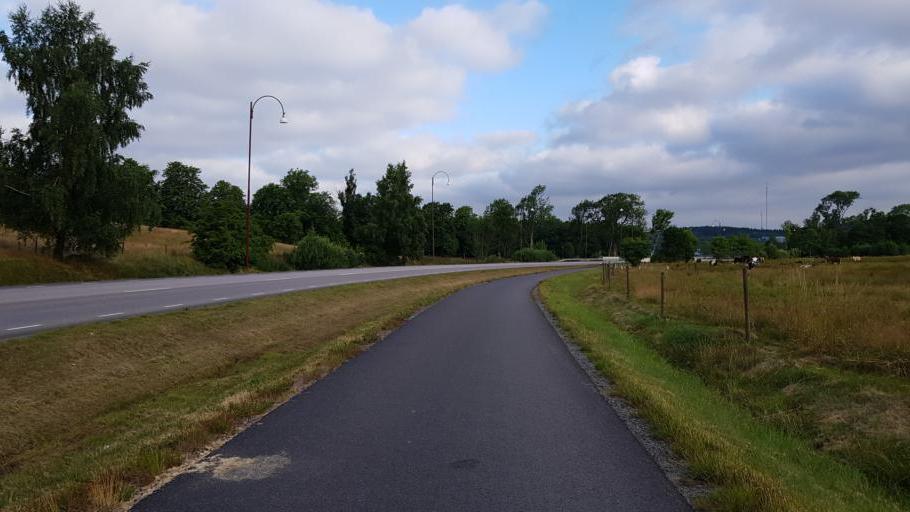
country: SE
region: Vaestra Goetaland
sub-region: Harryda Kommun
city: Molnlycke
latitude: 57.6606
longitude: 12.0942
